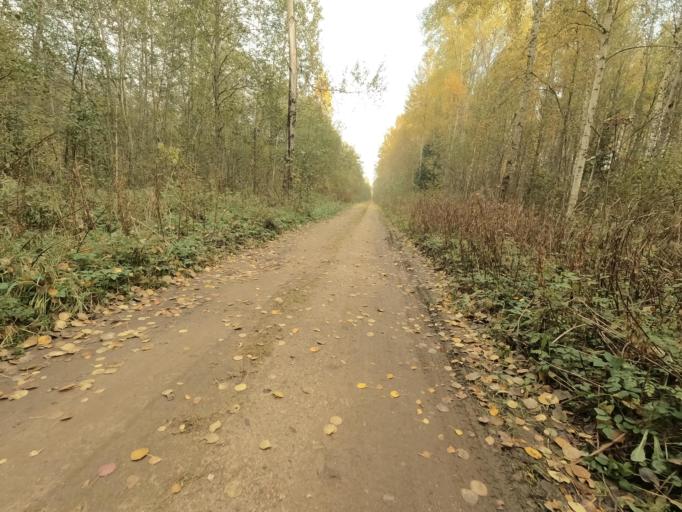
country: RU
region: Novgorod
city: Pankovka
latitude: 58.8800
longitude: 30.8246
